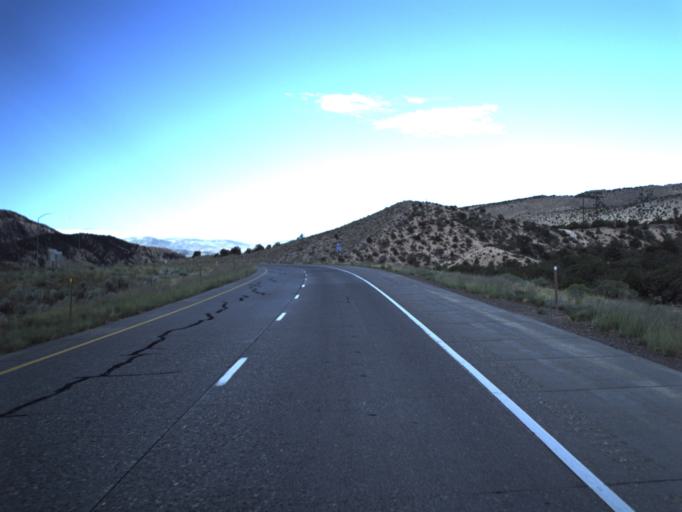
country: US
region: Utah
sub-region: Sevier County
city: Monroe
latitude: 38.5989
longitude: -112.2586
